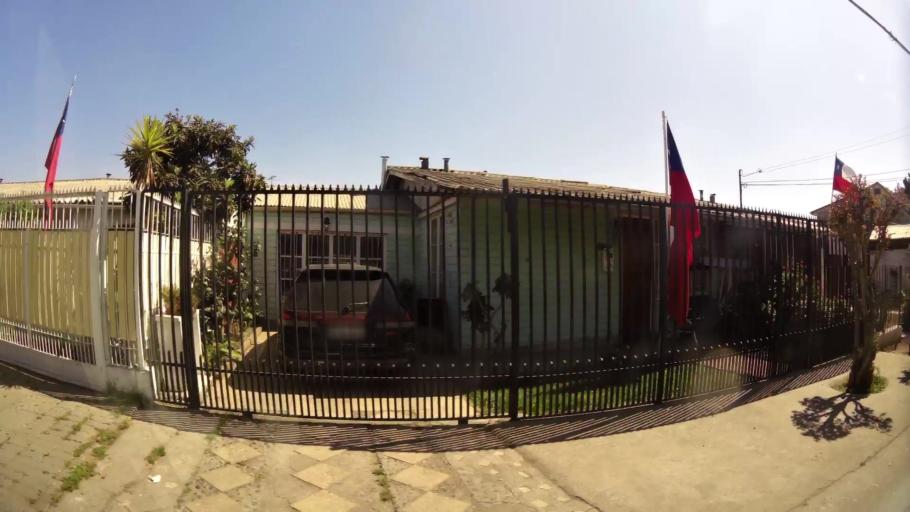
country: CL
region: Santiago Metropolitan
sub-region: Provincia de Santiago
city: Lo Prado
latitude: -33.5127
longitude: -70.7439
